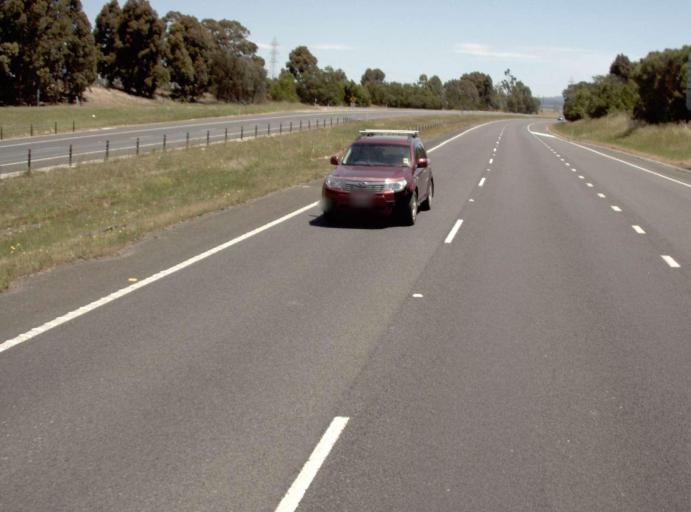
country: AU
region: Victoria
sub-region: Latrobe
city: Morwell
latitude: -38.2421
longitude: 146.4050
